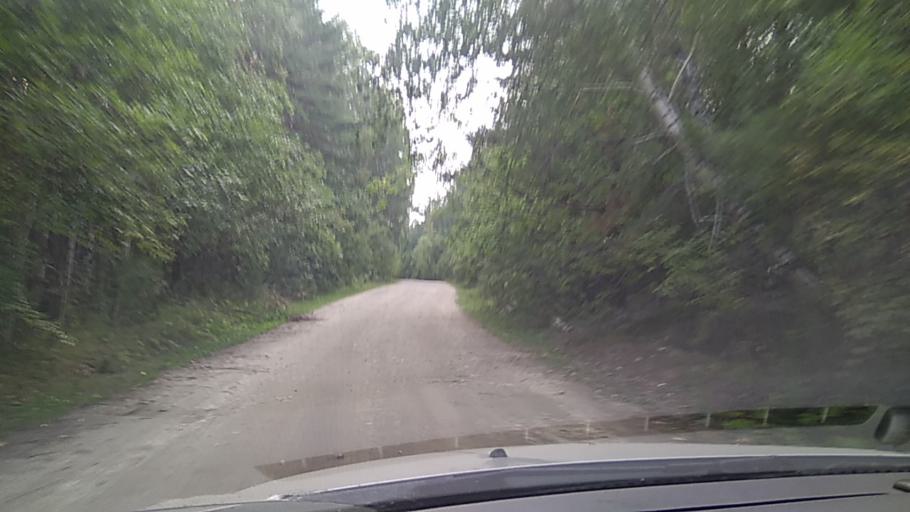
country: RU
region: Chelyabinsk
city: Kyshtym
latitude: 55.6773
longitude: 60.5886
